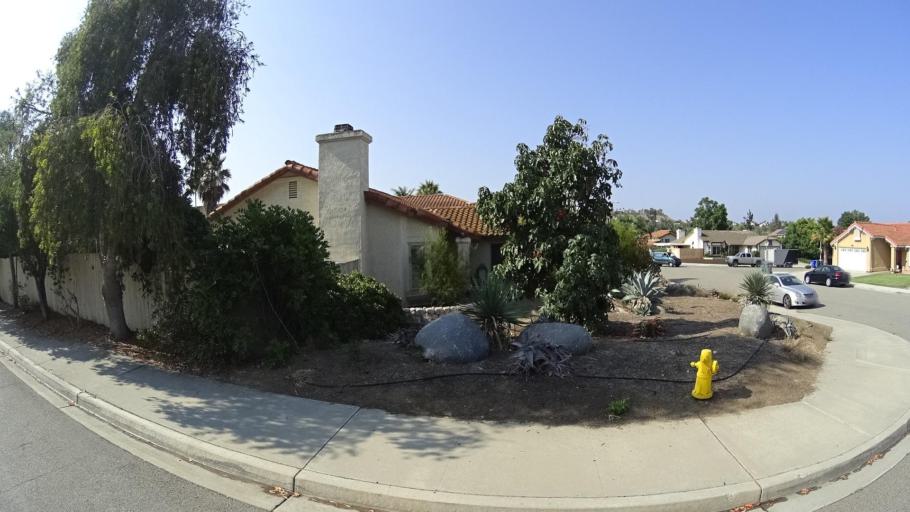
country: US
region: California
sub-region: San Diego County
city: Vista
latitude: 33.2412
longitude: -117.2671
